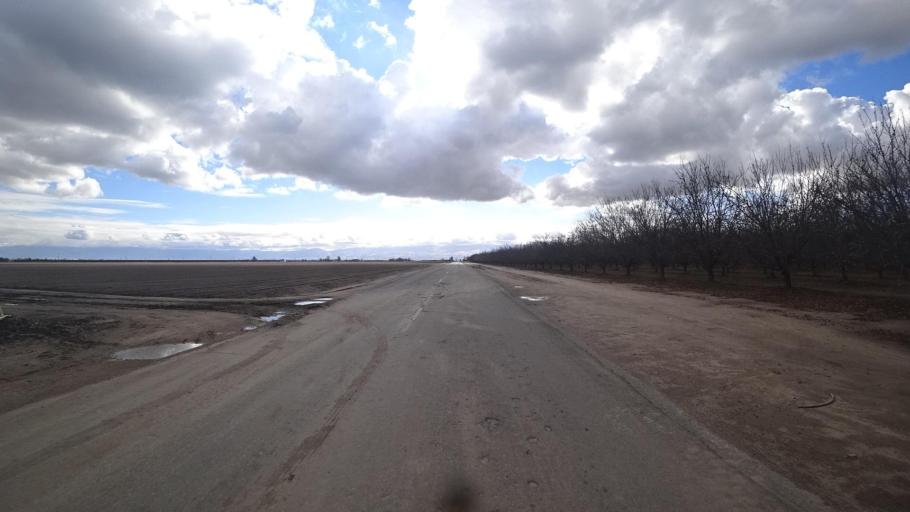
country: US
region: California
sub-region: Kern County
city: Greenfield
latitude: 35.2197
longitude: -119.0569
